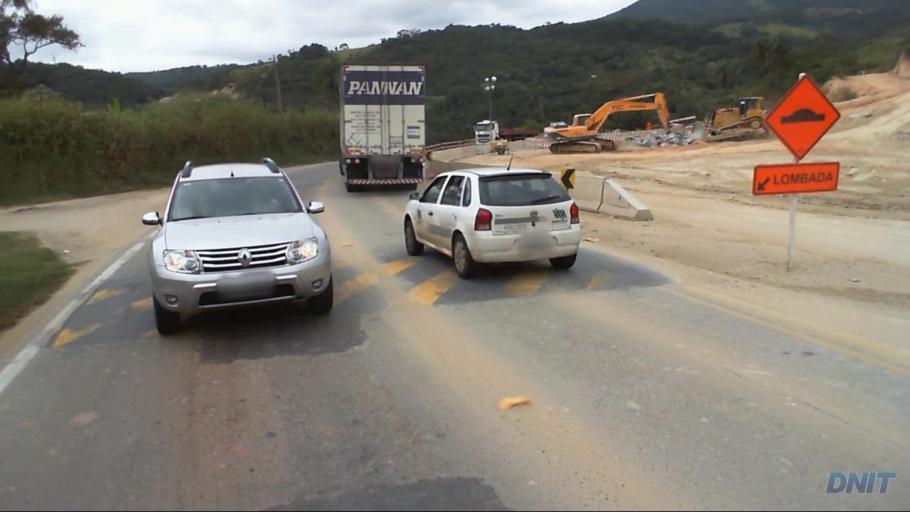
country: BR
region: Minas Gerais
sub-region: Caete
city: Caete
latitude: -19.7834
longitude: -43.6671
